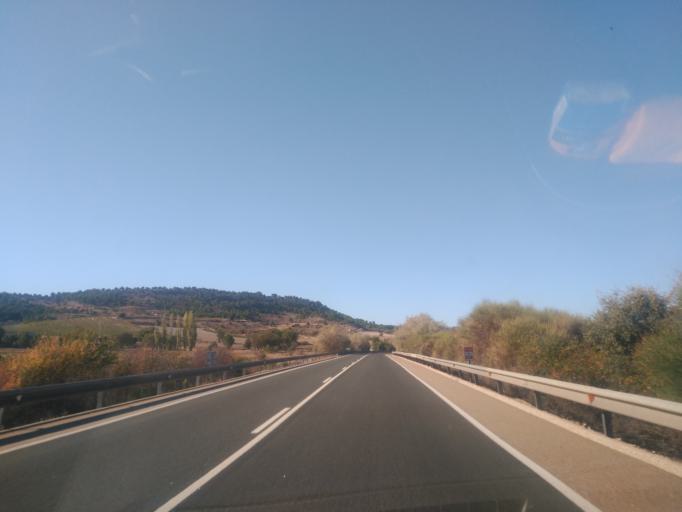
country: ES
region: Castille and Leon
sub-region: Provincia de Valladolid
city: Quintanilla de Onesimo
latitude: 41.6216
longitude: -4.3554
